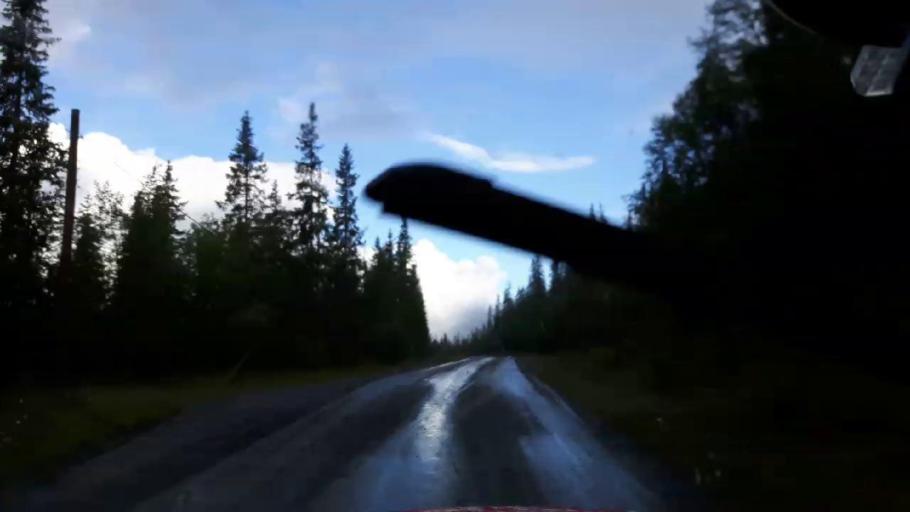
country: NO
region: Nordland
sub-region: Hattfjelldal
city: Hattfjelldal
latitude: 64.8654
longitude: 14.8912
